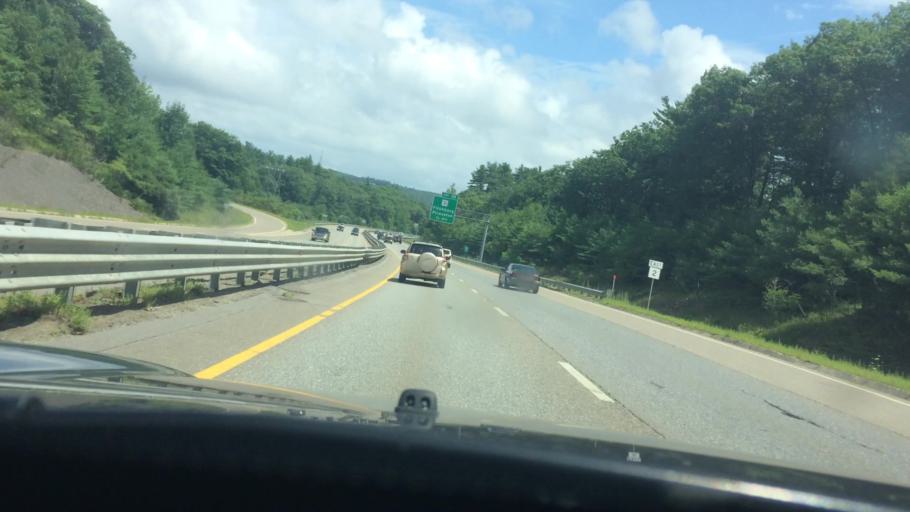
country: US
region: Massachusetts
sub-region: Worcester County
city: Westminster
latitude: 42.5472
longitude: -71.8661
